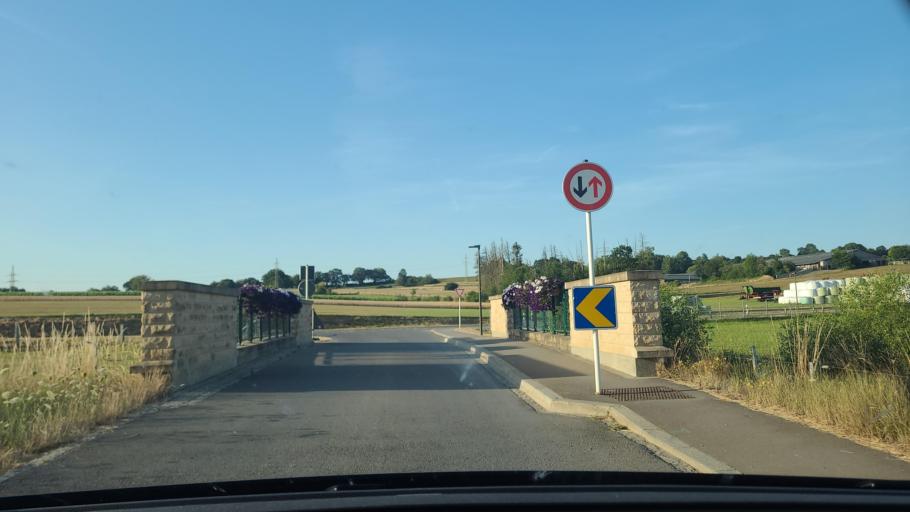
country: LU
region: Luxembourg
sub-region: Canton de Capellen
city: Garnich
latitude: 49.6137
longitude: 5.9585
